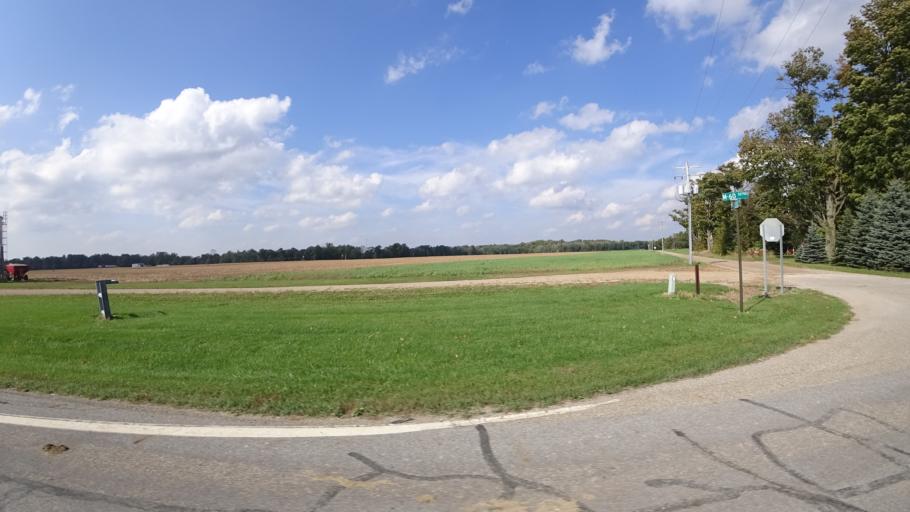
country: US
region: Michigan
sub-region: Saint Joseph County
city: Colon
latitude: 42.0403
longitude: -85.3175
